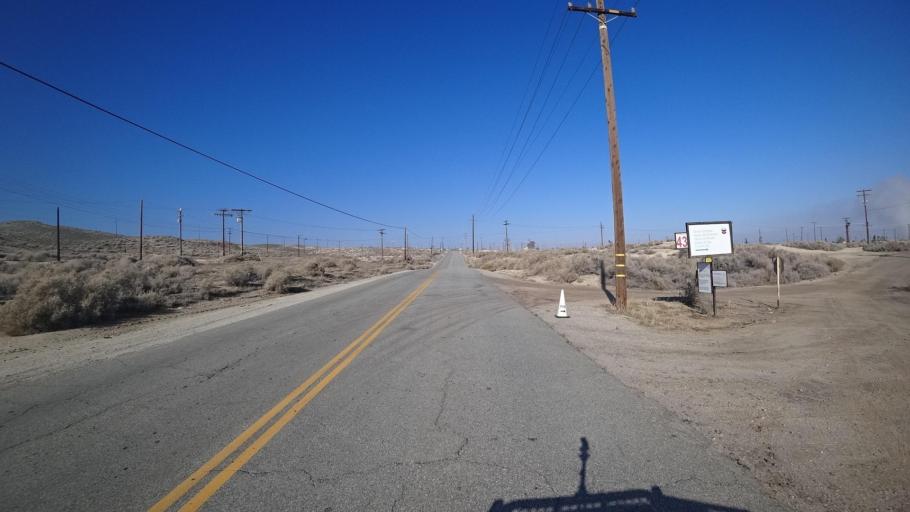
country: US
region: California
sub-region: Kern County
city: Taft Heights
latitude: 35.1980
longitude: -119.5895
